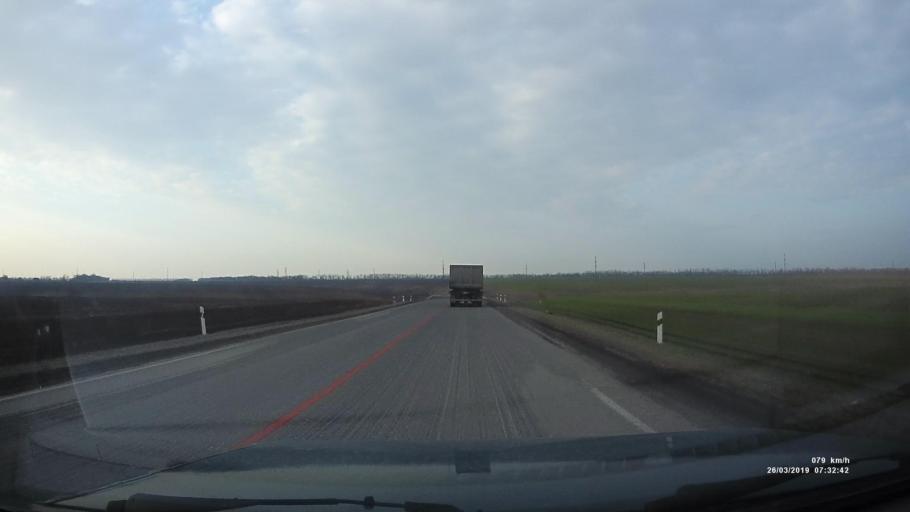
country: RU
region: Rostov
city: Novobessergenovka
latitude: 47.2230
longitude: 38.7757
